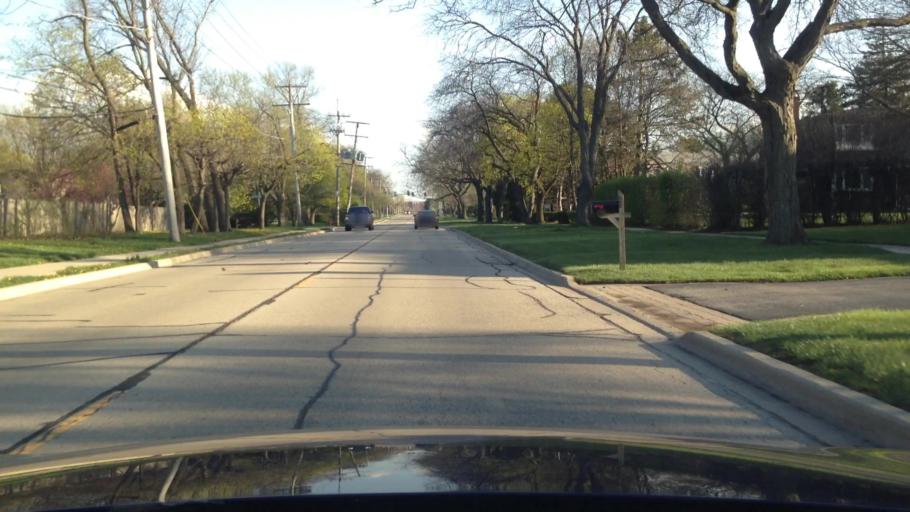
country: US
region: Illinois
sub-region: Lake County
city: Deerfield
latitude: 42.1624
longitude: -87.8673
